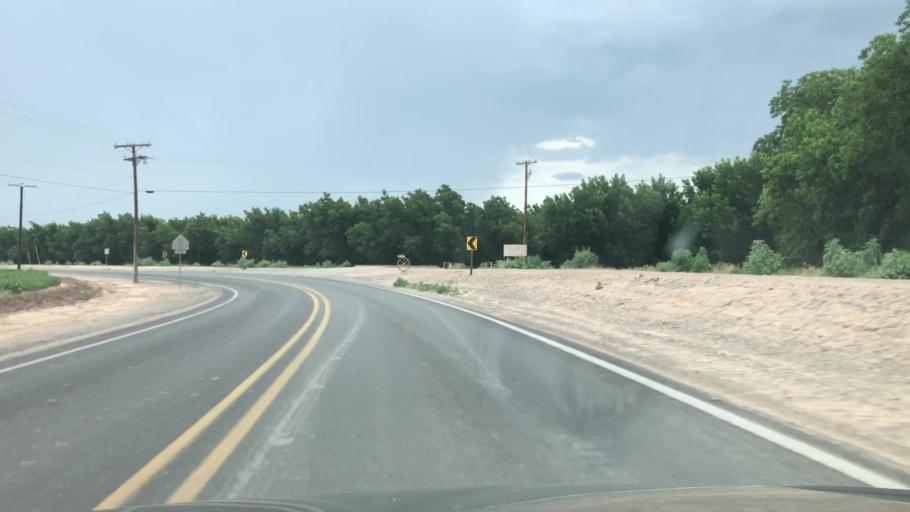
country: US
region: New Mexico
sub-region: Dona Ana County
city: La Union
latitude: 31.9856
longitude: -106.6497
